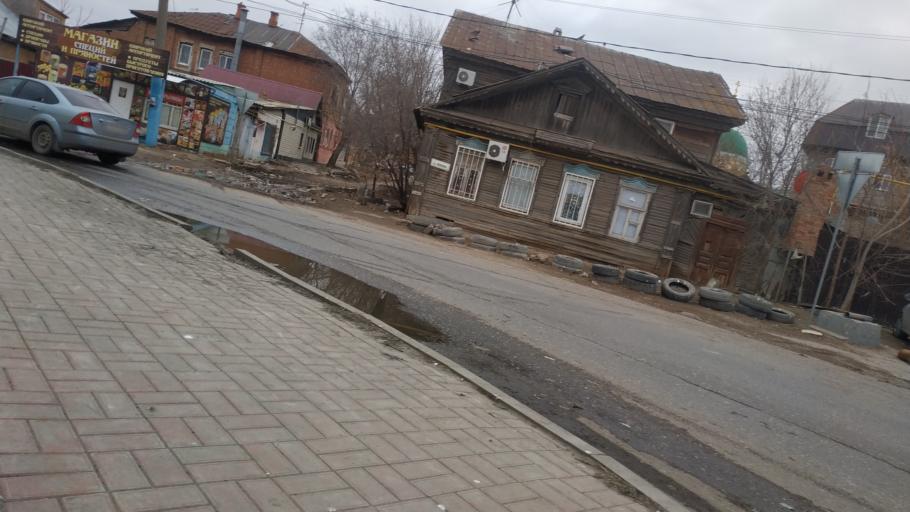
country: RU
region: Astrakhan
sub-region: Gorod Astrakhan'
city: Astrakhan'
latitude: 46.3422
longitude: 48.0235
